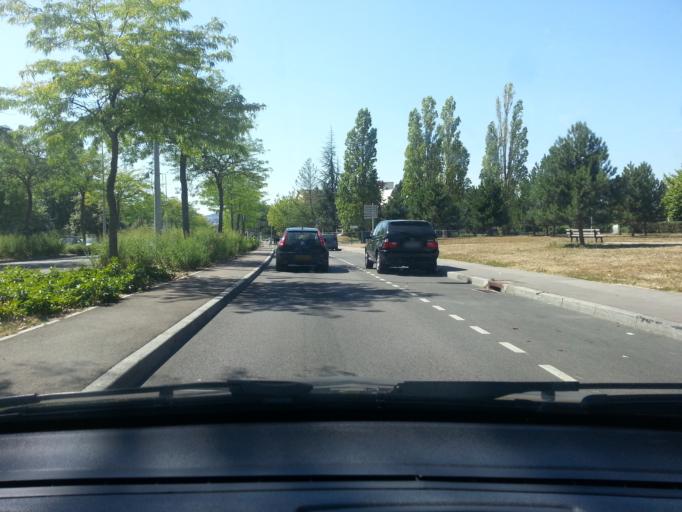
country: FR
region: Bourgogne
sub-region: Departement de la Cote-d'Or
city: Saint-Apollinaire
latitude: 47.3358
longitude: 5.0635
